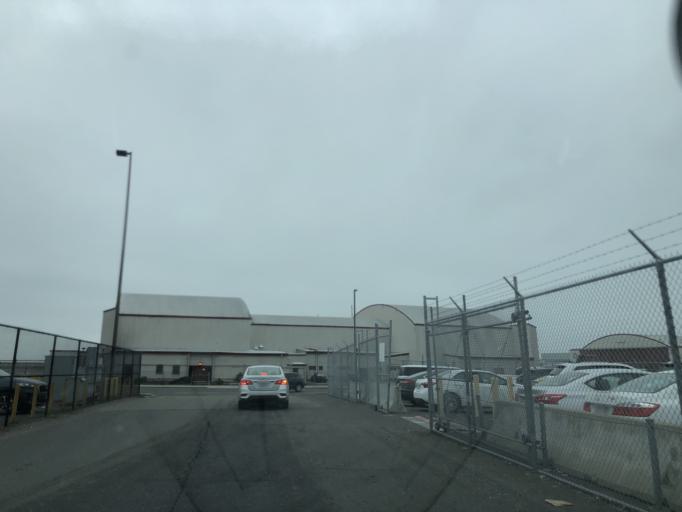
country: US
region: California
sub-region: Alameda County
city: Alameda
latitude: 37.7346
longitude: -122.2142
